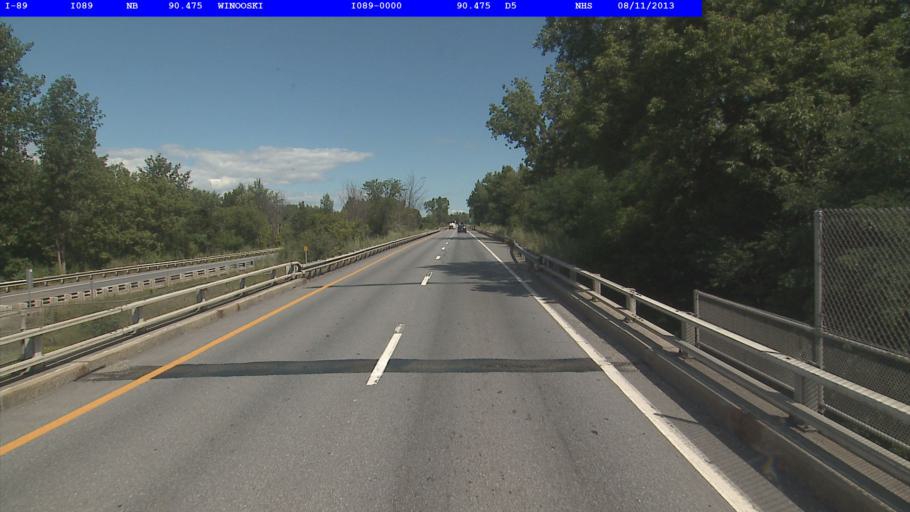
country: US
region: Vermont
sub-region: Chittenden County
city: Winooski
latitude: 44.4933
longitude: -73.1731
